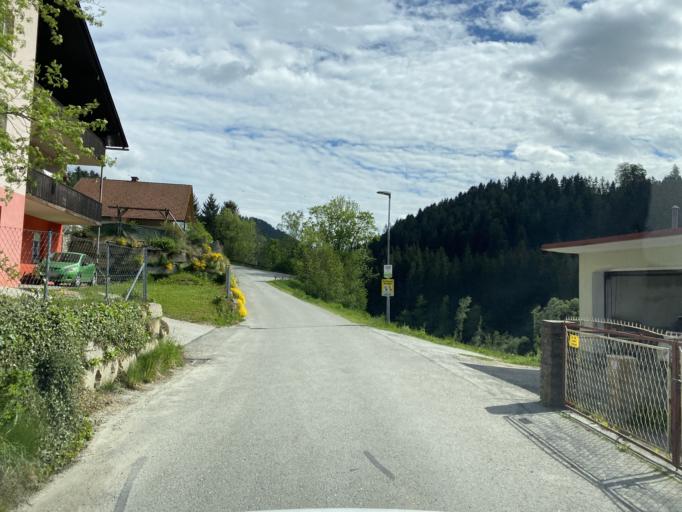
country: AT
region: Styria
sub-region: Politischer Bezirk Weiz
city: Birkfeld
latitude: 47.3492
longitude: 15.6993
